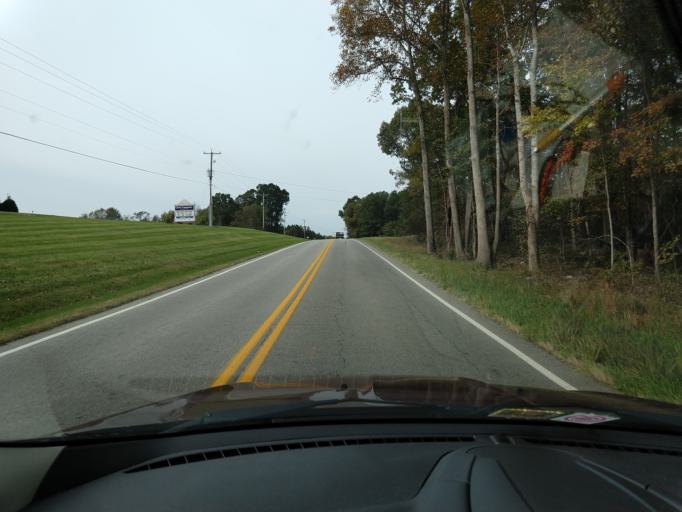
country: US
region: Virginia
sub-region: Franklin County
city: Union Hall
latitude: 36.9842
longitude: -79.6336
